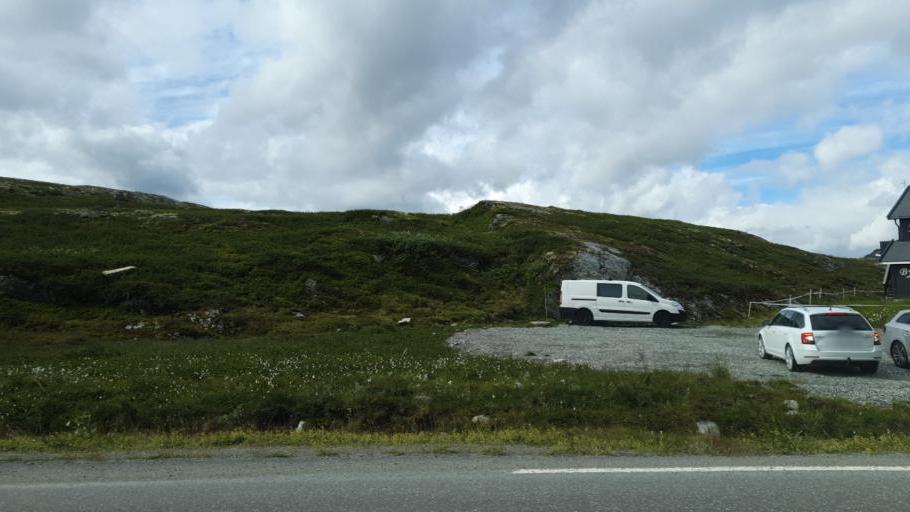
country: NO
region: Oppland
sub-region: Vang
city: Vang
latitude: 61.3306
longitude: 8.7955
